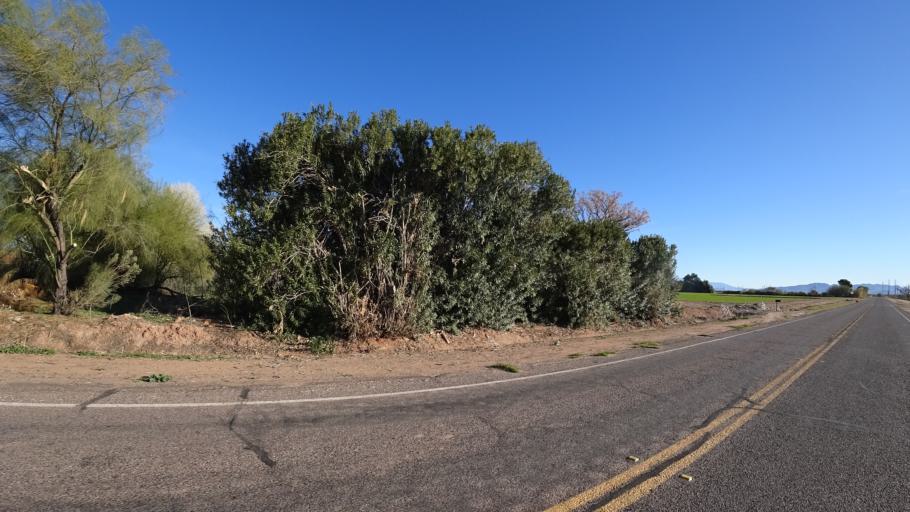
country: US
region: Arizona
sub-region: Maricopa County
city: Mesa
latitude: 33.4806
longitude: -111.8393
